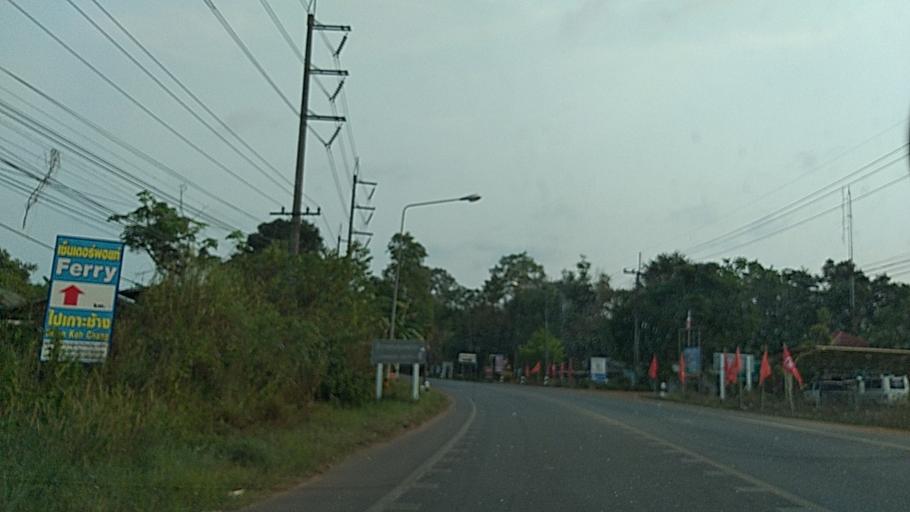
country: TH
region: Trat
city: Laem Ngop
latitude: 12.2176
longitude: 102.3078
